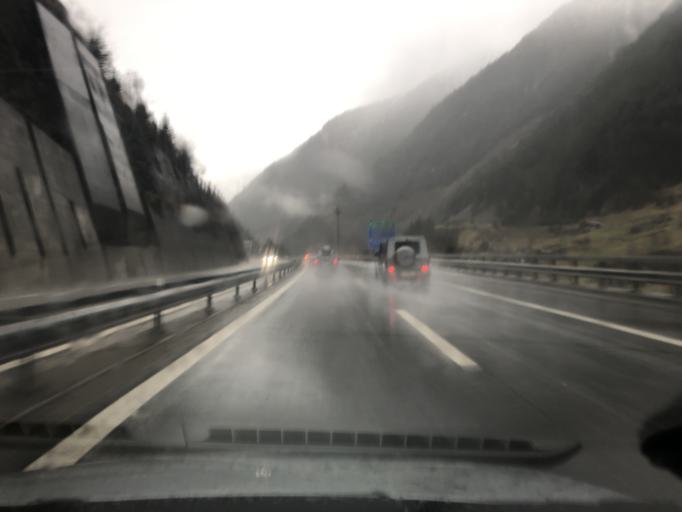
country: CH
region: Uri
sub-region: Uri
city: Andermatt
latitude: 46.6938
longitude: 8.5963
